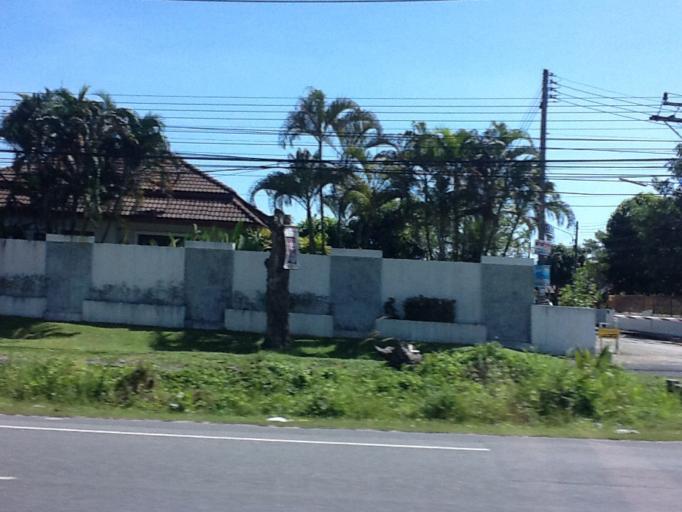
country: TH
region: Phuket
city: Thalang
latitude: 8.0093
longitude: 98.3973
